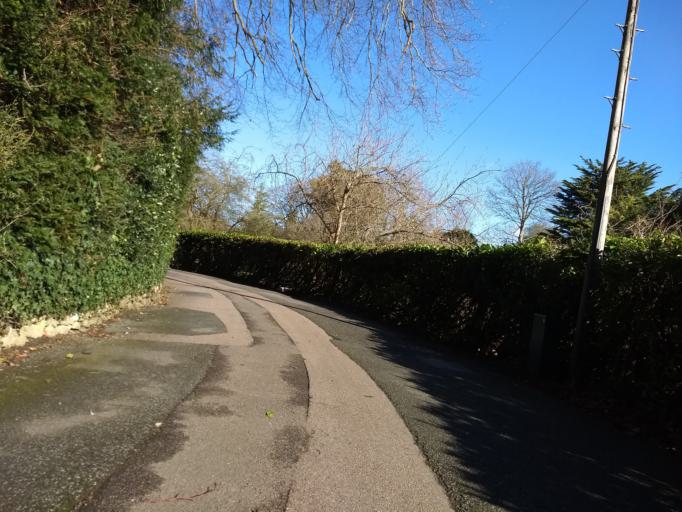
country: GB
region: England
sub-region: Isle of Wight
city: Ryde
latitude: 50.7294
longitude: -1.1857
